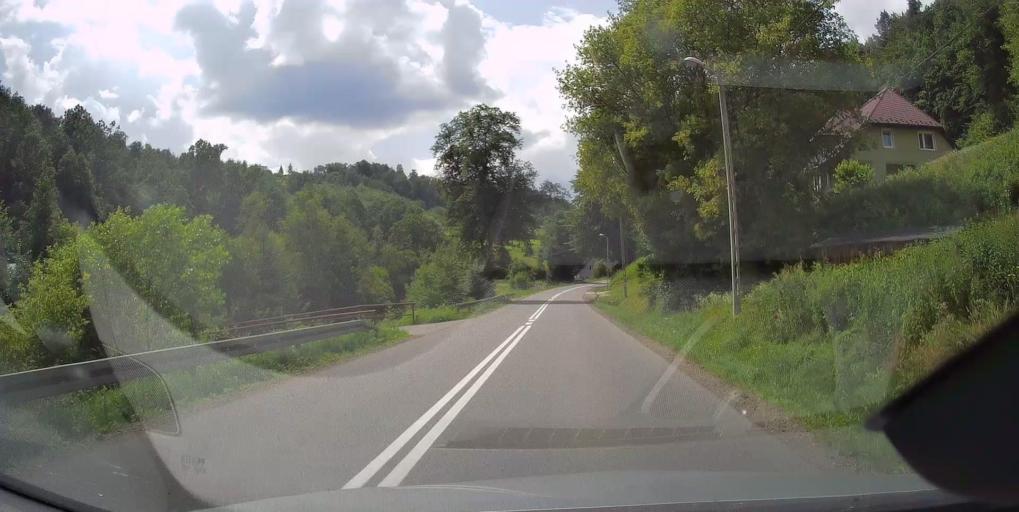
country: PL
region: Lesser Poland Voivodeship
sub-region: Powiat nowosadecki
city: Nowy Sacz
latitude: 49.6497
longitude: 20.7217
